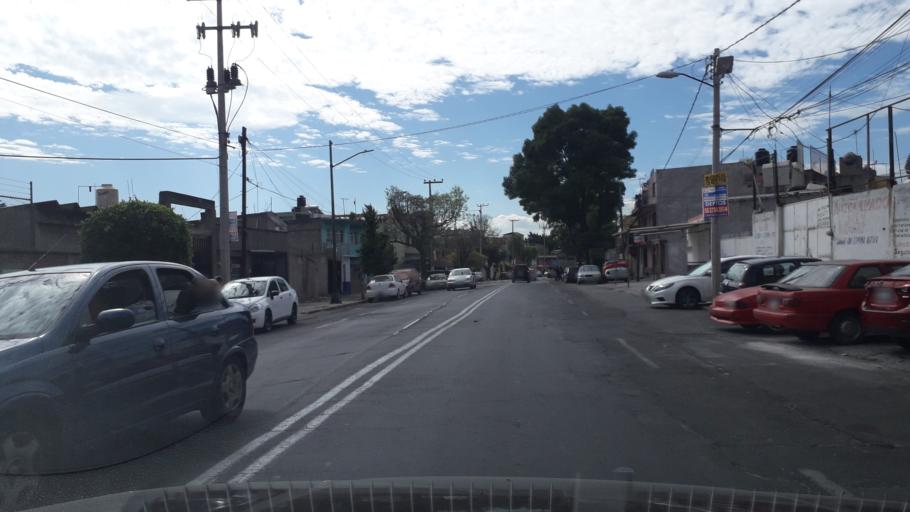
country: MX
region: Mexico City
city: Gustavo A. Madero
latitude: 19.5006
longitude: -99.0936
